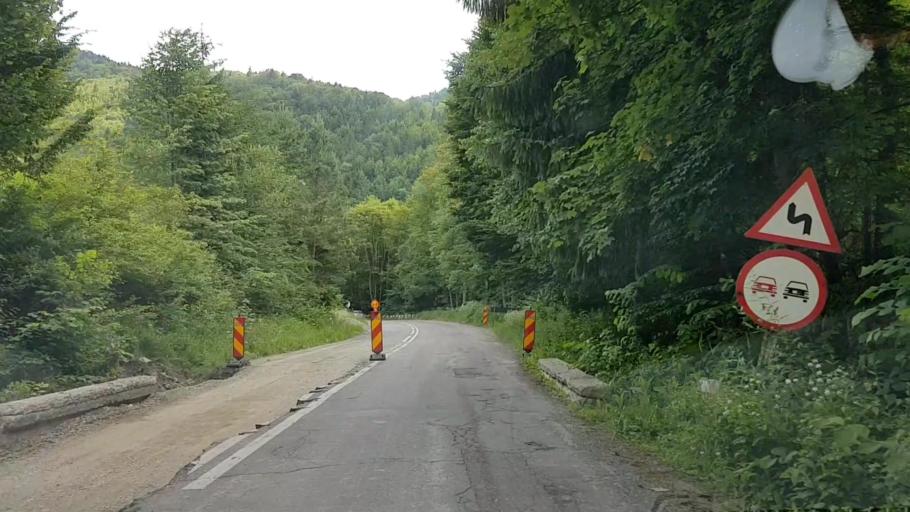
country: RO
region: Neamt
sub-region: Comuna Pangarati
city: Pangarati
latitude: 46.9373
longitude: 26.1267
